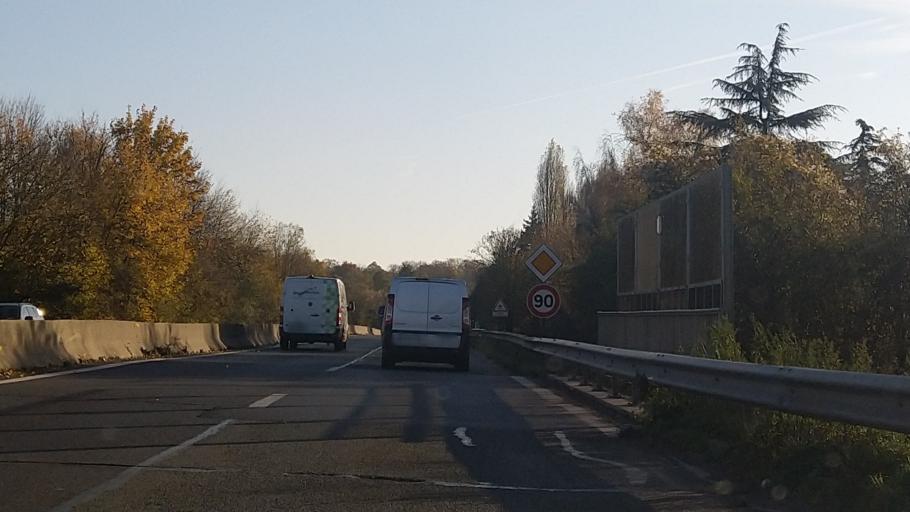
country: FR
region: Ile-de-France
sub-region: Departement du Val-d'Oise
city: Domont
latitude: 49.0312
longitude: 2.3466
